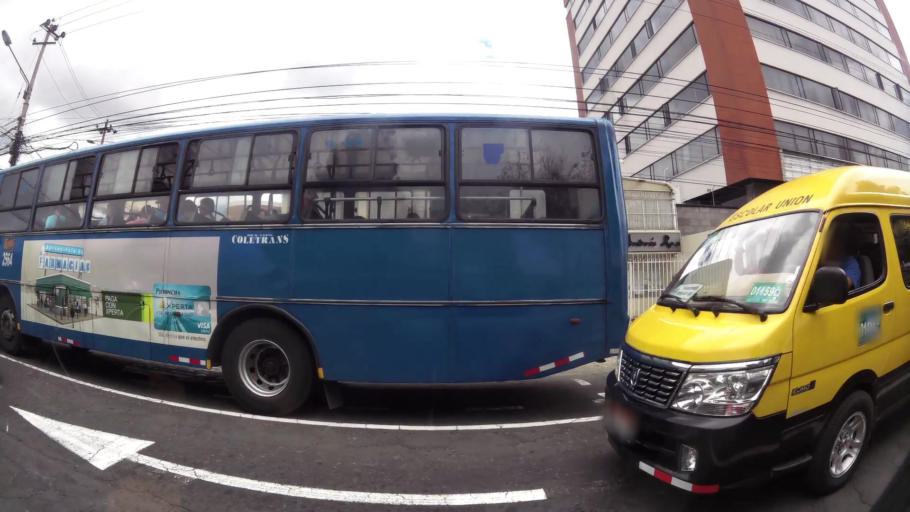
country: EC
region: Pichincha
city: Quito
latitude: -0.1677
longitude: -78.4795
